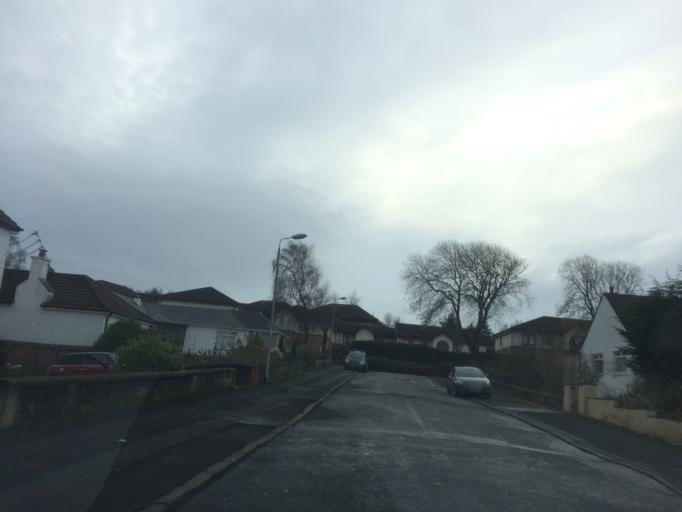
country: GB
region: Scotland
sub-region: East Renfrewshire
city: Giffnock
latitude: 55.8073
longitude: -4.2892
